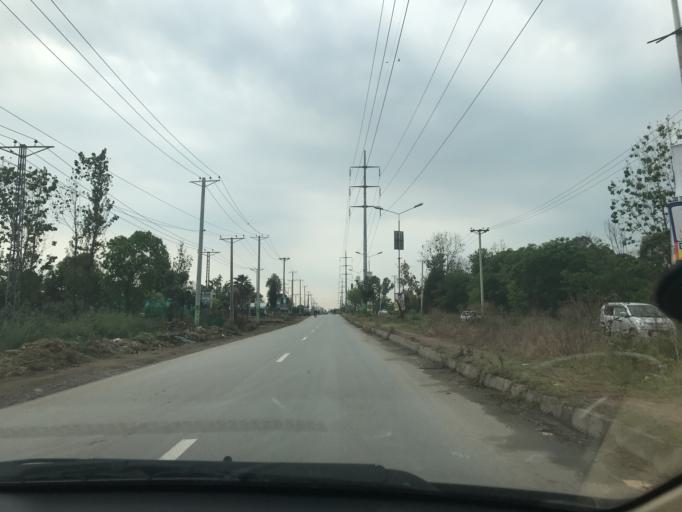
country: PK
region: Punjab
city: Rawalpindi
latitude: 33.6781
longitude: 73.1505
